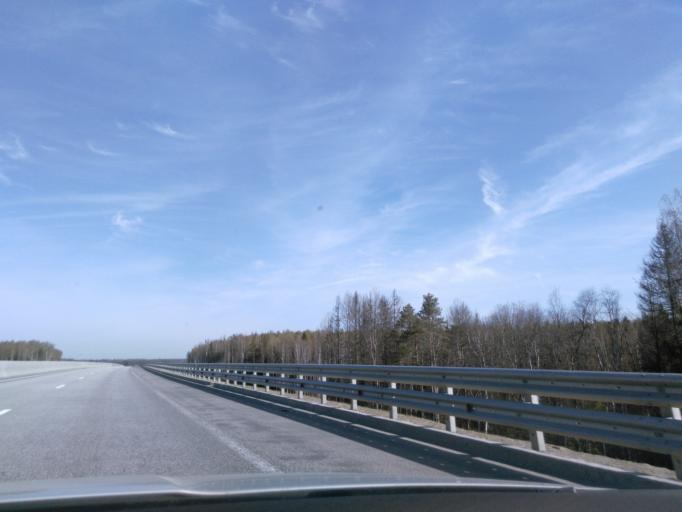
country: RU
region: Moskovskaya
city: Mendeleyevo
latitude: 56.0782
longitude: 37.2117
